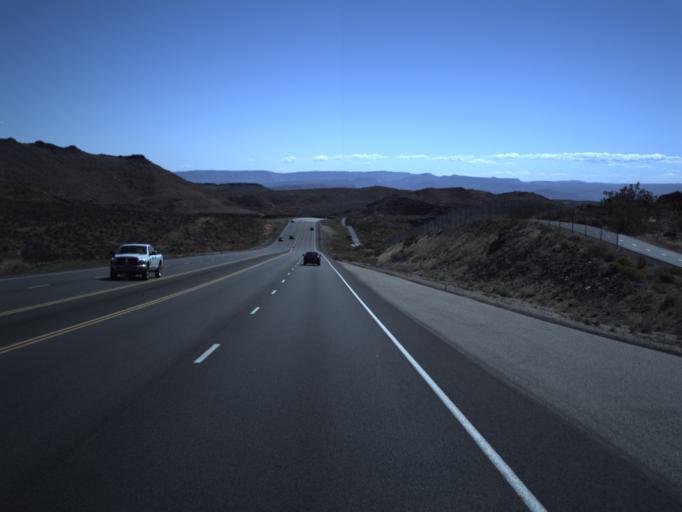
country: US
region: Utah
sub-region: Washington County
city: Santa Clara
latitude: 37.1692
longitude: -113.6173
